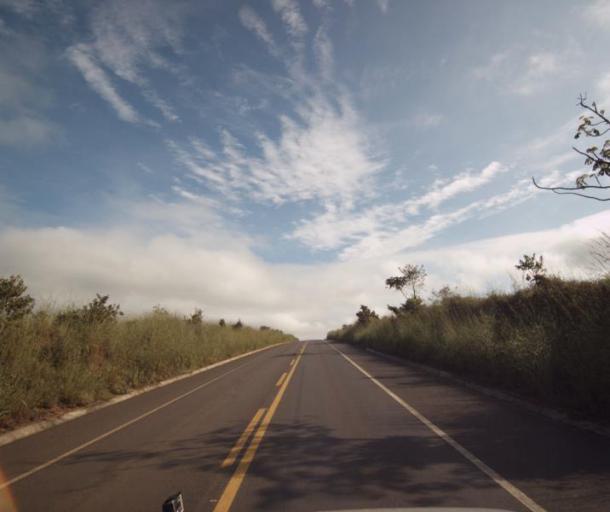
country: BR
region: Goias
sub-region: Padre Bernardo
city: Padre Bernardo
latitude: -15.4322
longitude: -48.6207
